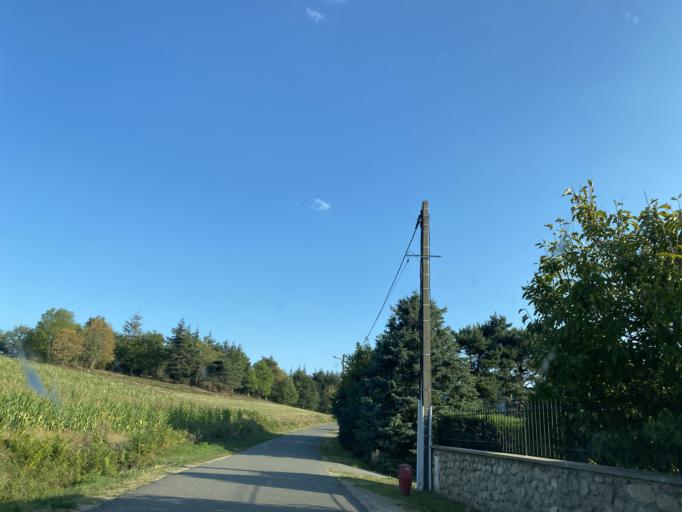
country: FR
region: Rhone-Alpes
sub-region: Departement de la Loire
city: Noiretable
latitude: 45.8114
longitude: 3.7632
